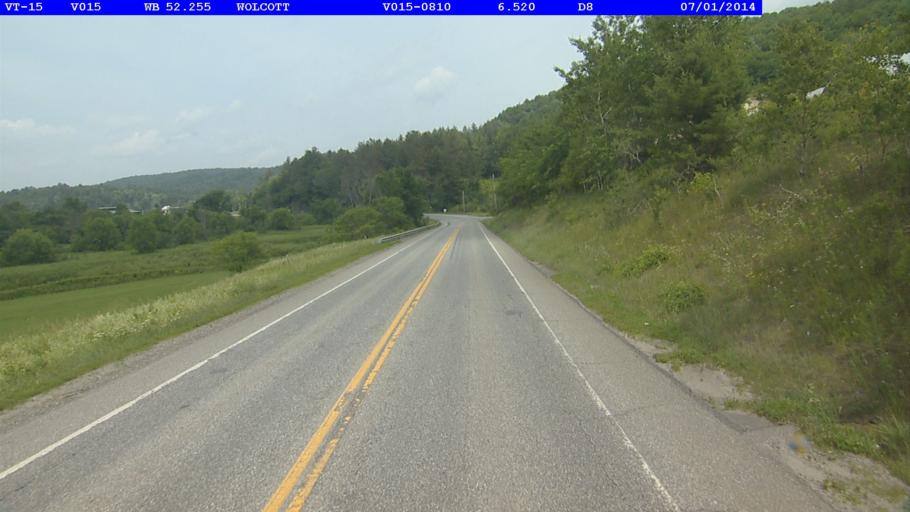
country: US
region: Vermont
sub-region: Caledonia County
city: Hardwick
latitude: 44.5309
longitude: -72.4248
